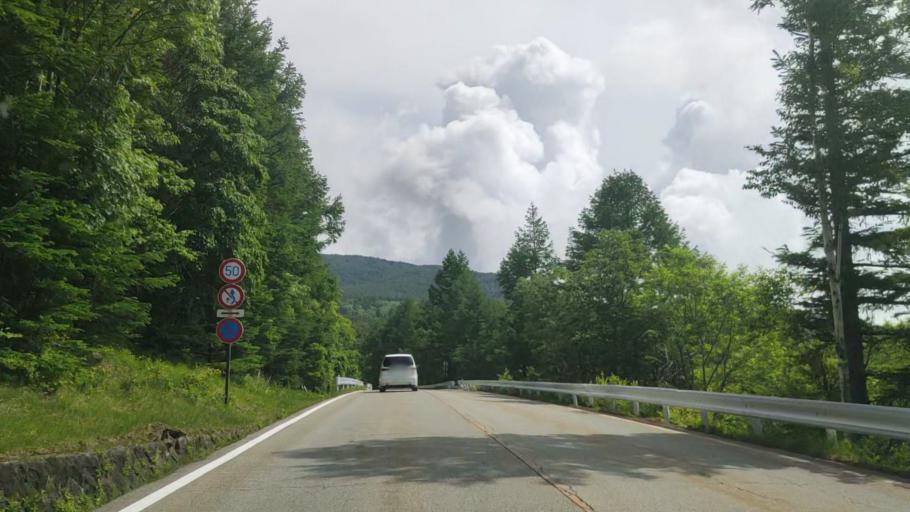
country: JP
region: Yamanashi
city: Fujikawaguchiko
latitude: 35.4132
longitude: 138.6998
